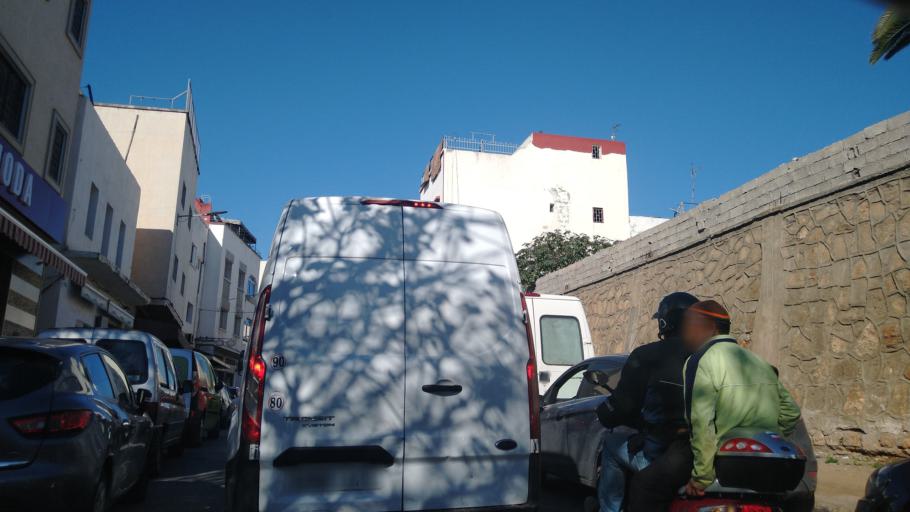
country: MA
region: Rabat-Sale-Zemmour-Zaer
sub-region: Rabat
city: Rabat
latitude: 34.0351
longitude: -6.8204
